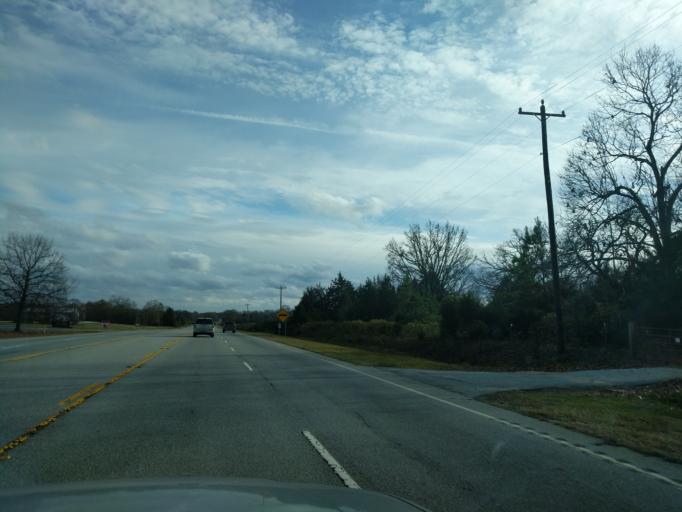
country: US
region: South Carolina
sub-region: Anderson County
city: Honea Path
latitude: 34.5214
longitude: -82.3127
